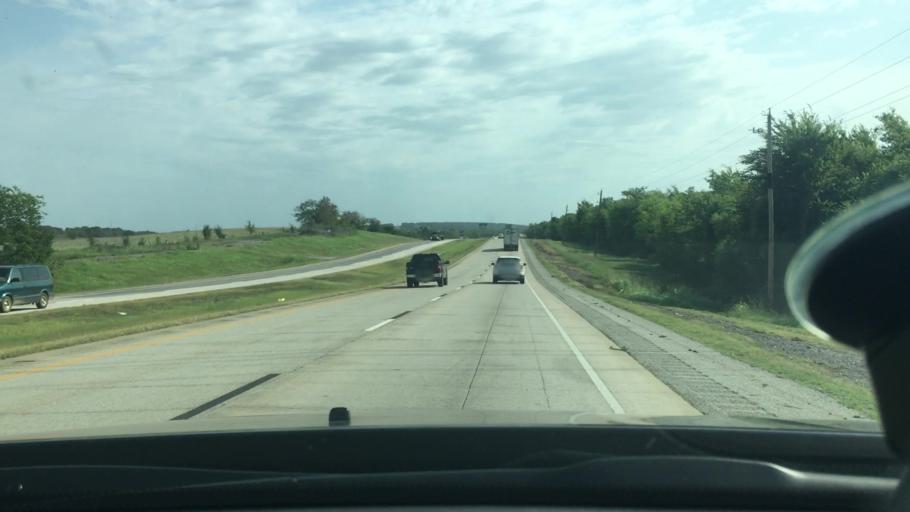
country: US
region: Oklahoma
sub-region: Atoka County
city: Atoka
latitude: 34.4101
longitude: -96.1076
